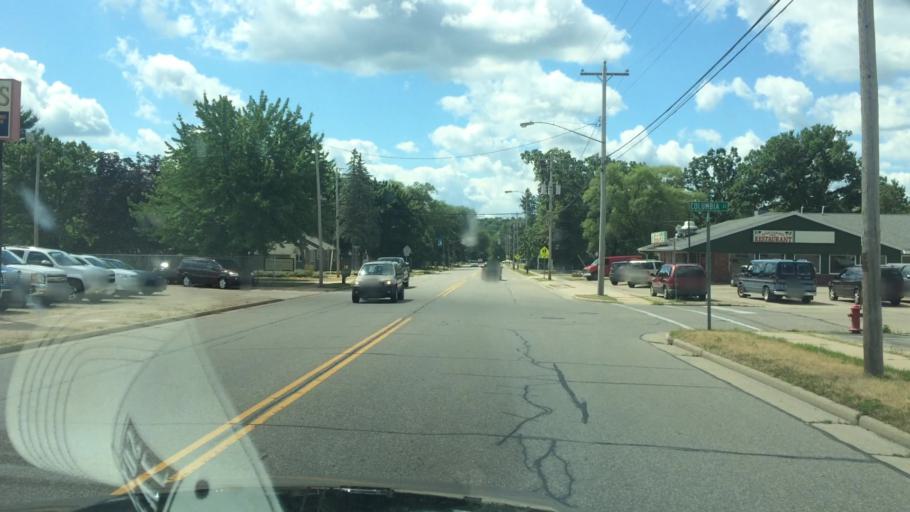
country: US
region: Wisconsin
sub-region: Waupaca County
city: Waupaca
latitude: 44.3495
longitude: -89.0722
